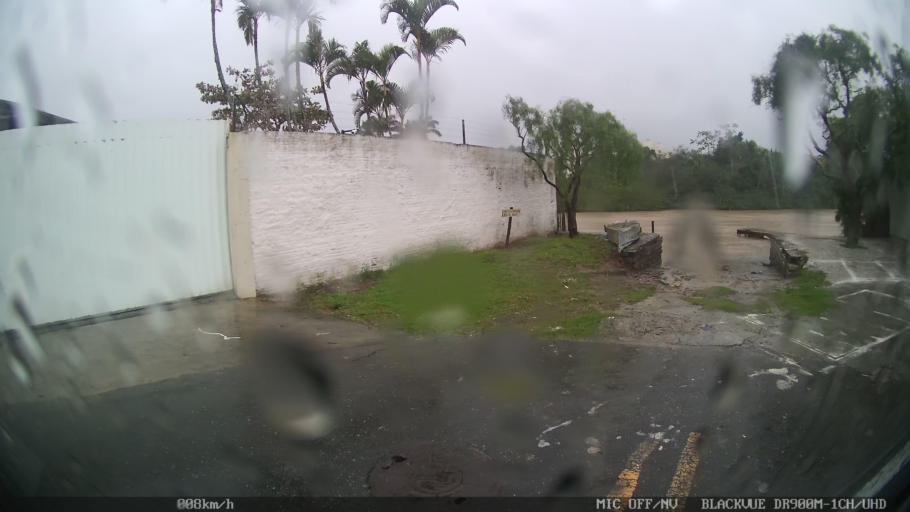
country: BR
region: Santa Catarina
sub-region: Balneario Camboriu
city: Balneario Camboriu
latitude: -27.0155
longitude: -48.6321
